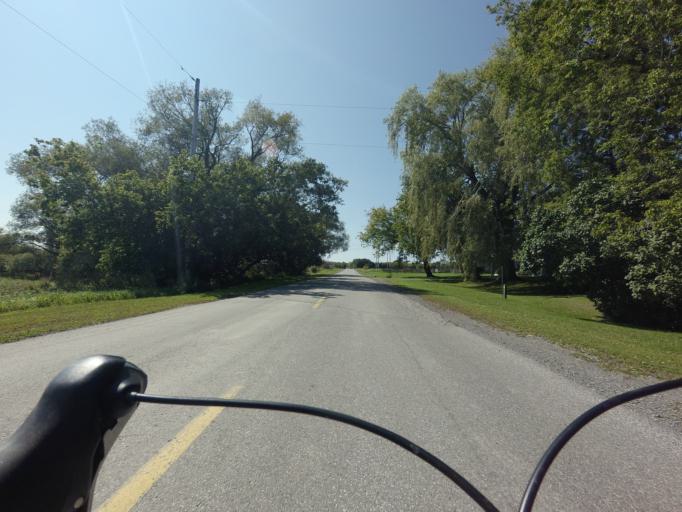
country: CA
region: Ontario
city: Bells Corners
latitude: 45.3809
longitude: -76.0091
